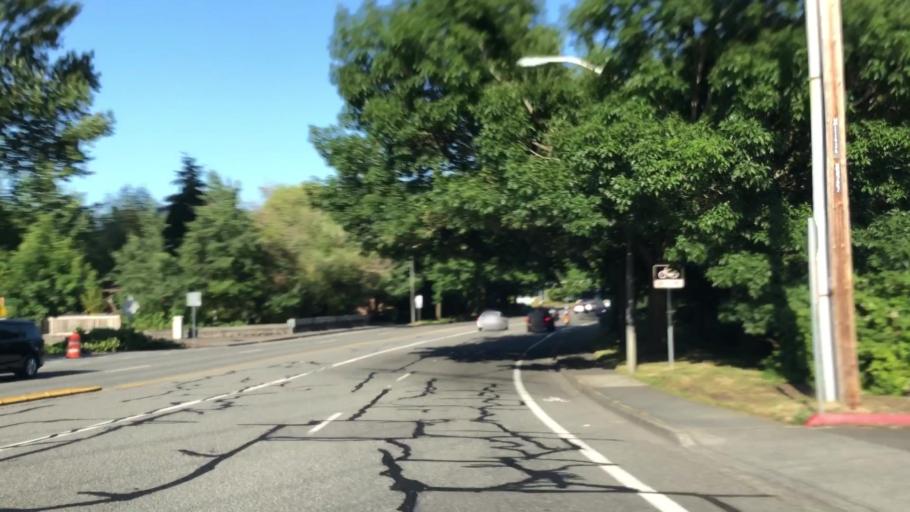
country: US
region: Washington
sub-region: King County
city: Bothell
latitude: 47.7690
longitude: -122.1876
